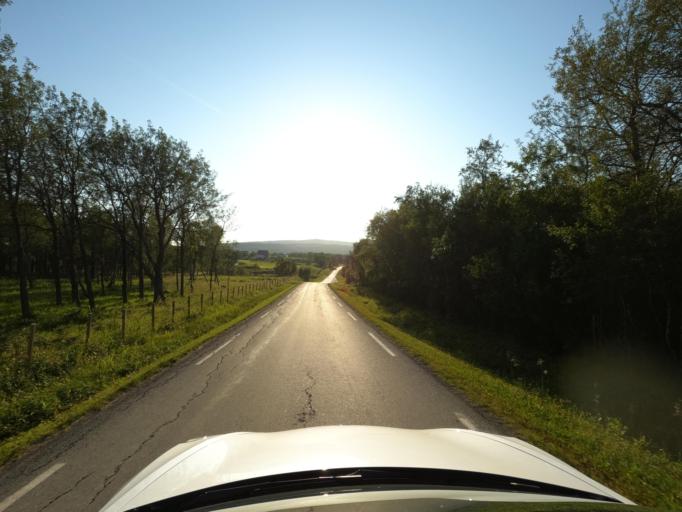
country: NO
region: Troms
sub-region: Skanland
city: Evenskjer
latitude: 68.4636
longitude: 16.6676
